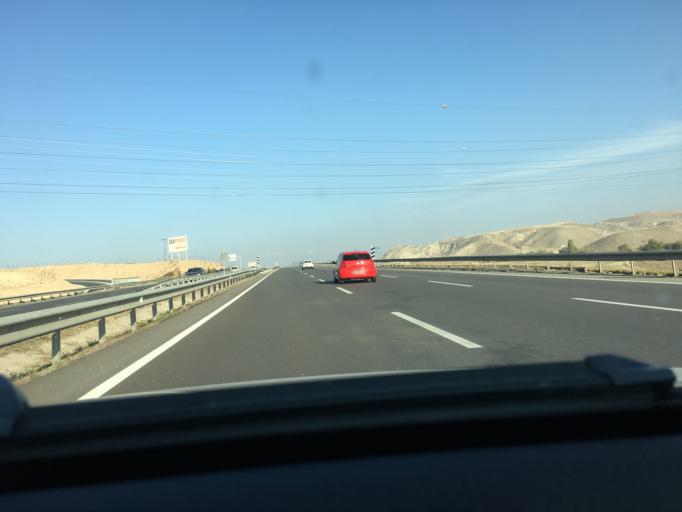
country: TR
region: Ankara
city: Temelli
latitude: 39.7563
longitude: 32.4494
